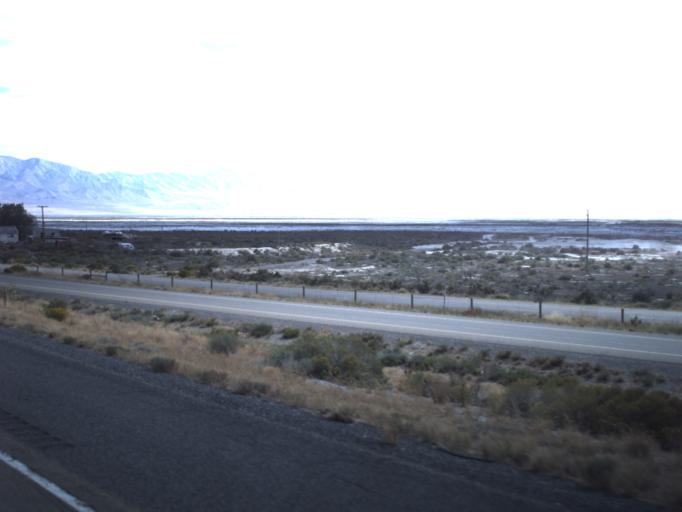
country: US
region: Utah
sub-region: Tooele County
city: Grantsville
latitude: 40.7617
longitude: -112.7797
